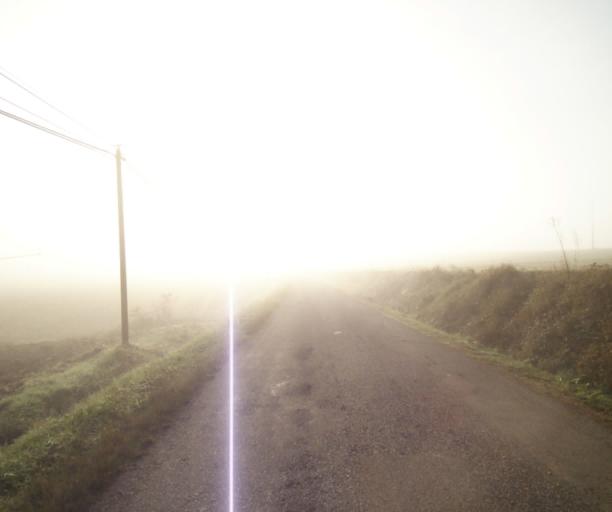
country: FR
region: Midi-Pyrenees
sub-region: Departement du Tarn-et-Garonne
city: Nohic
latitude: 43.9033
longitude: 1.4684
